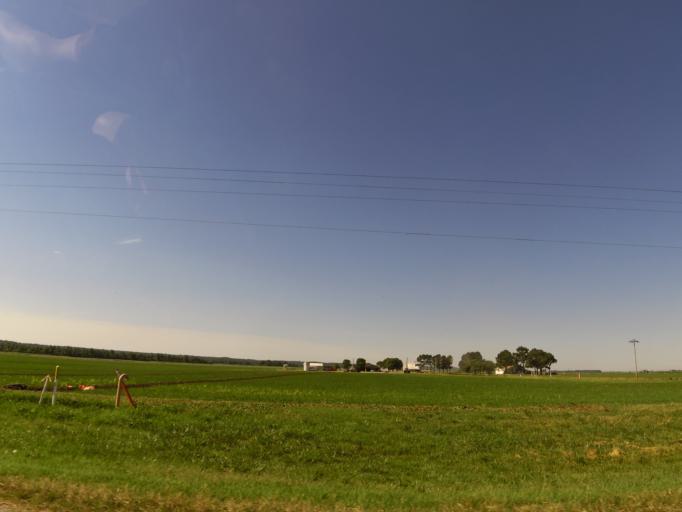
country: US
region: Arkansas
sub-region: Clay County
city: Piggott
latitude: 36.4343
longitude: -90.3706
